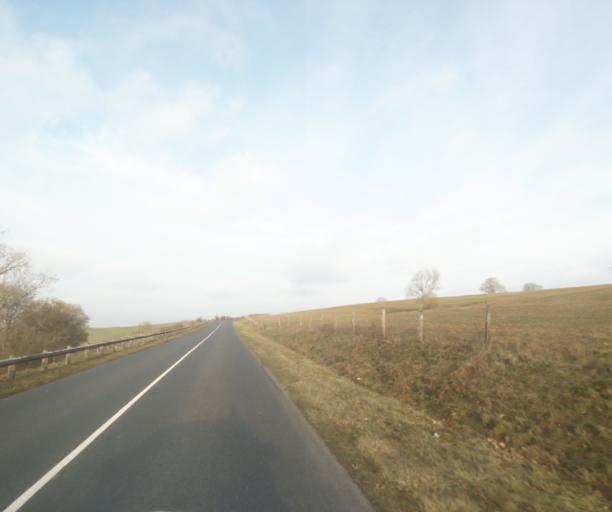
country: FR
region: Champagne-Ardenne
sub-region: Departement de la Marne
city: Sermaize-les-Bains
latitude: 48.7250
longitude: 4.9385
